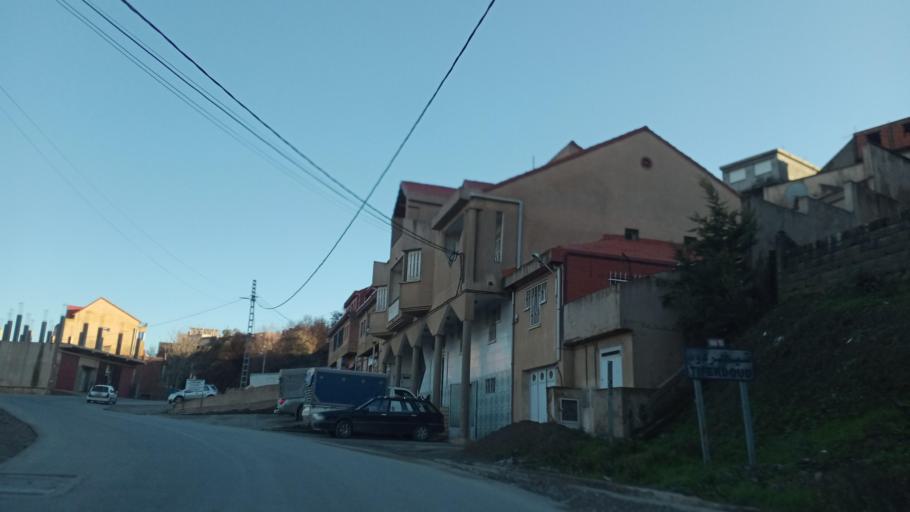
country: DZ
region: Tizi Ouzou
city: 'Ain el Hammam
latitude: 36.5598
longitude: 4.3242
